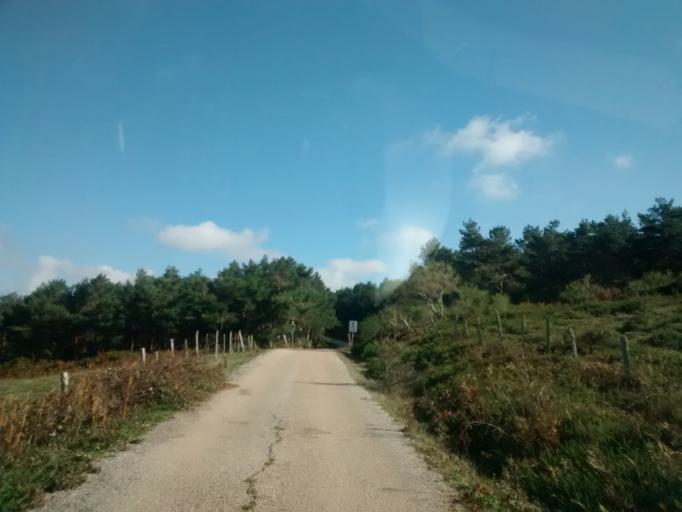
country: ES
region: Castille and Leon
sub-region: Provincia de Burgos
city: Arija
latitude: 42.9255
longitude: -3.9879
